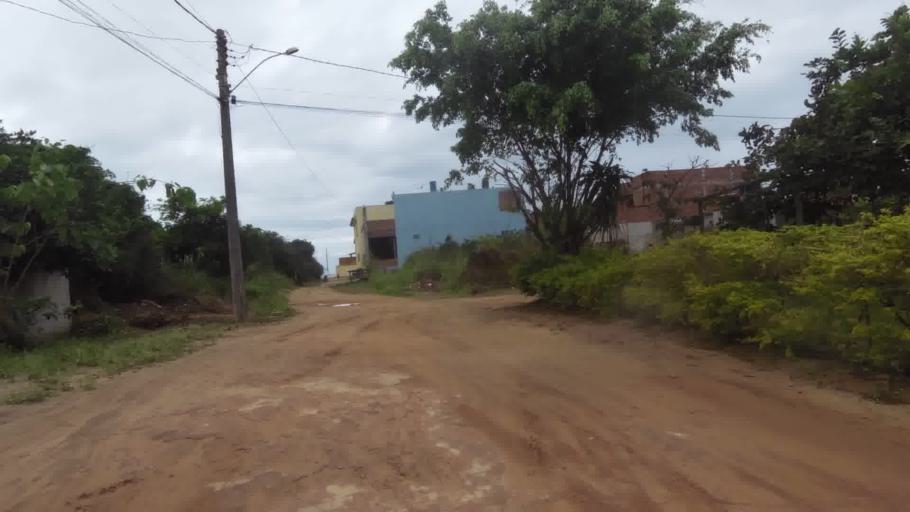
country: BR
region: Espirito Santo
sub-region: Marataizes
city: Marataizes
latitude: -21.0616
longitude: -40.8364
